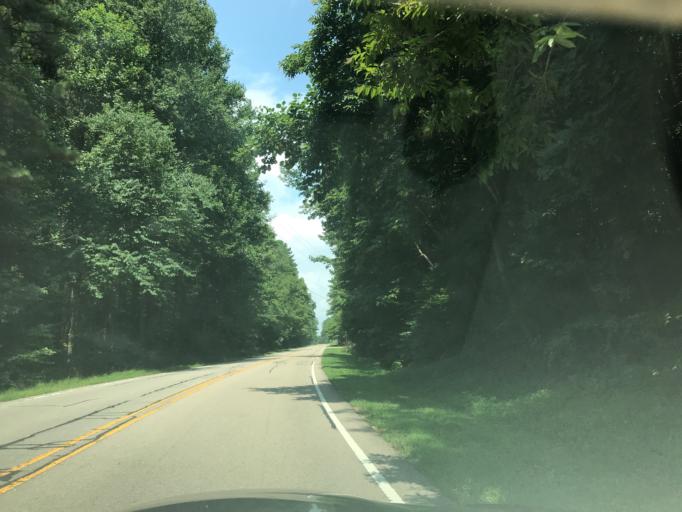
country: US
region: North Carolina
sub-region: Wake County
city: Cary
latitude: 35.8357
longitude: -78.7216
